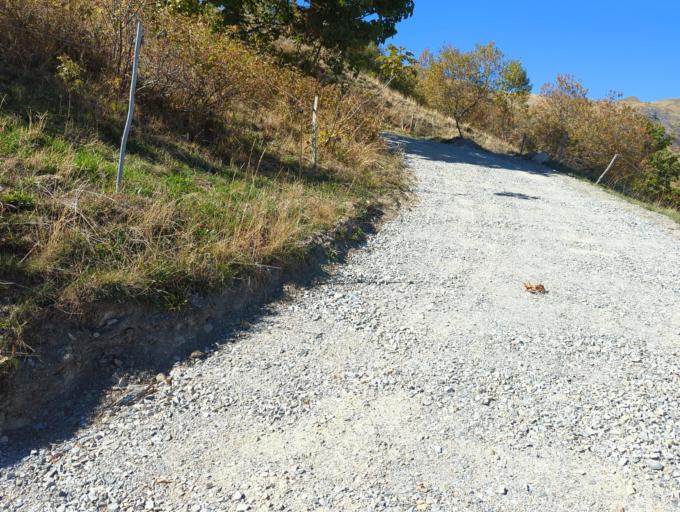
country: FR
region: Rhone-Alpes
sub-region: Departement de la Savoie
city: Saint-Jean-de-Maurienne
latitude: 45.2582
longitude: 6.2723
